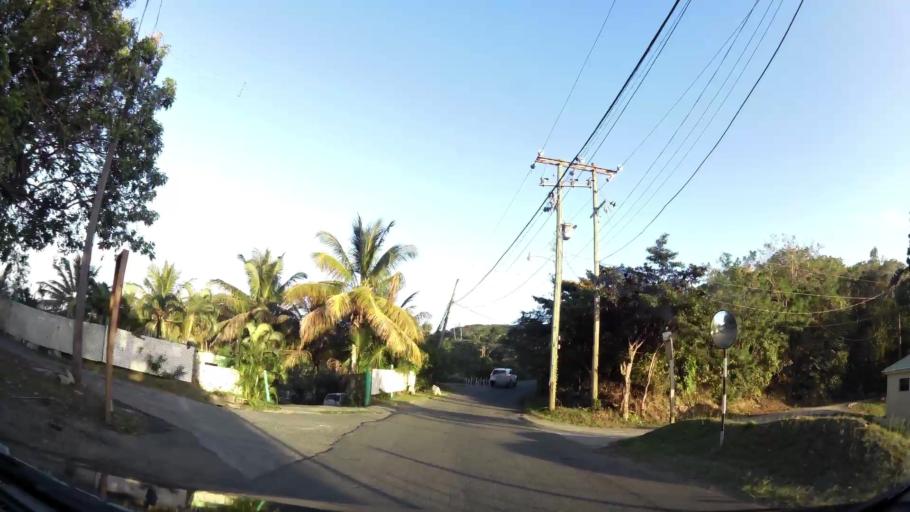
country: VG
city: Road Town
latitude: 18.4390
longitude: -64.6218
